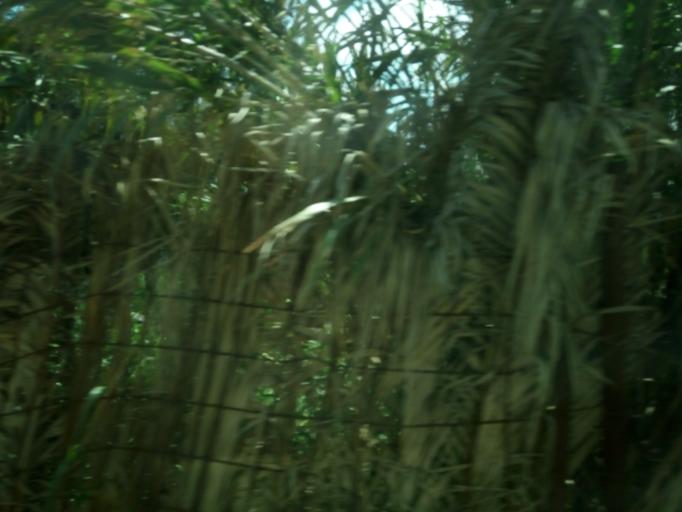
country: DZ
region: Tipaza
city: Saoula
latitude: 36.7296
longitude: 2.9966
